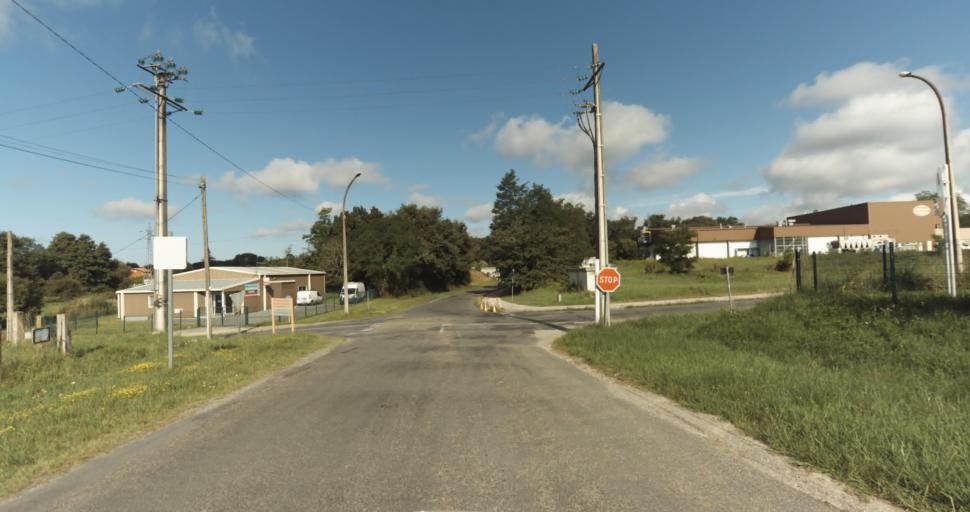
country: FR
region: Aquitaine
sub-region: Departement de la Gironde
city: Bazas
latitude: 44.4384
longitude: -0.2365
